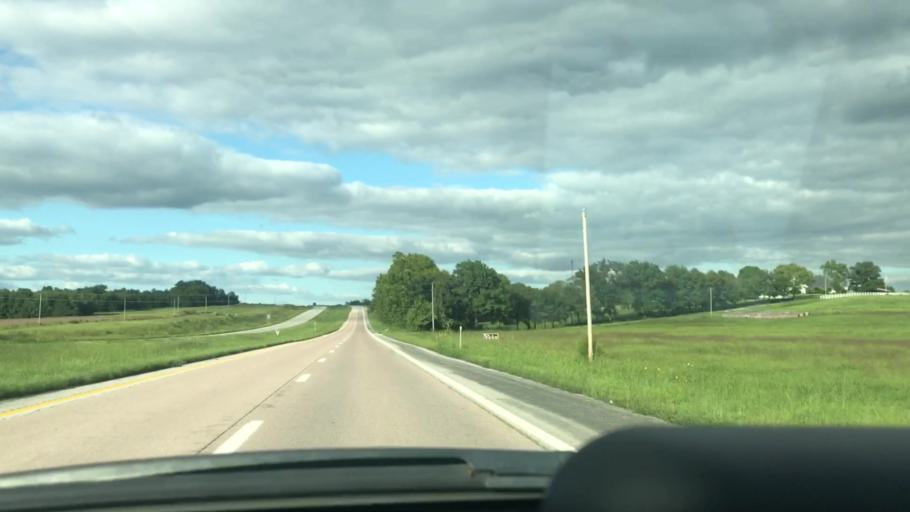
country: US
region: Missouri
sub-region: Benton County
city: Lincoln
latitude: 38.4500
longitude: -93.2857
